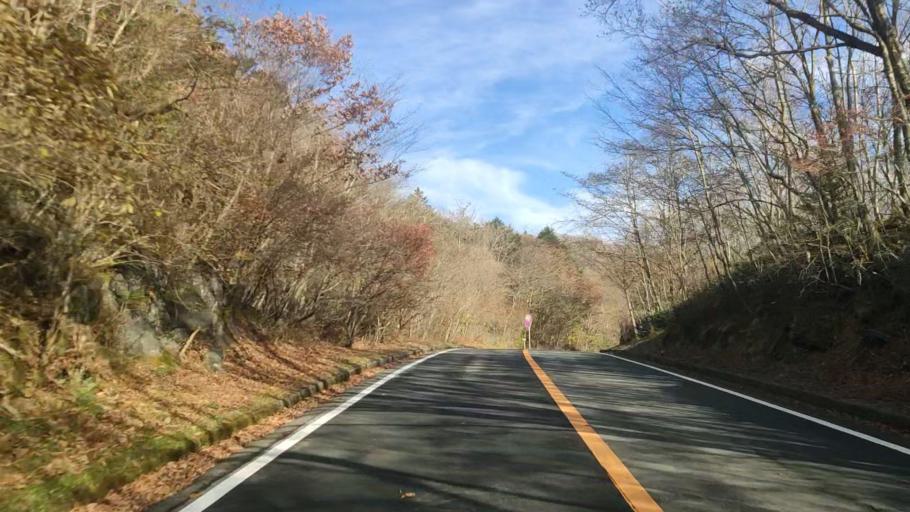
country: JP
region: Shizuoka
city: Fuji
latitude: 35.3024
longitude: 138.7369
